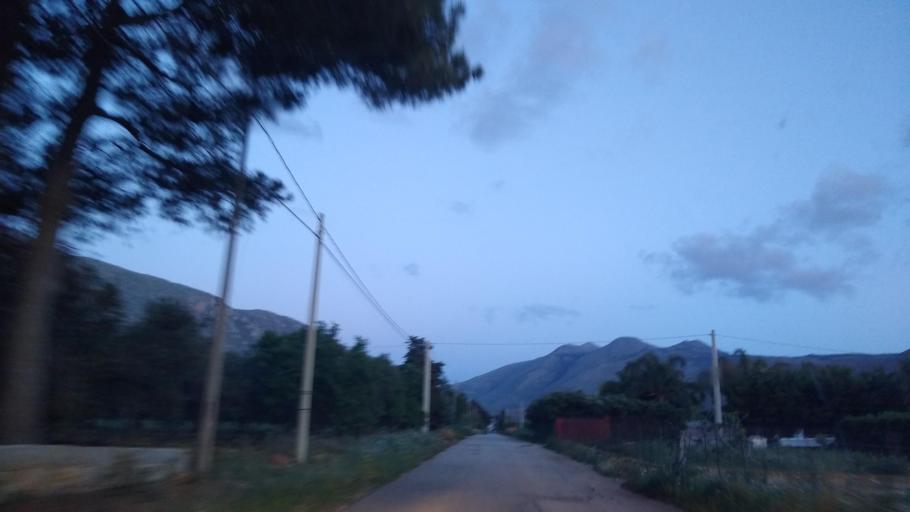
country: IT
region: Sicily
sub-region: Trapani
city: Castelluzzo
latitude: 38.1082
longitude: 12.7274
